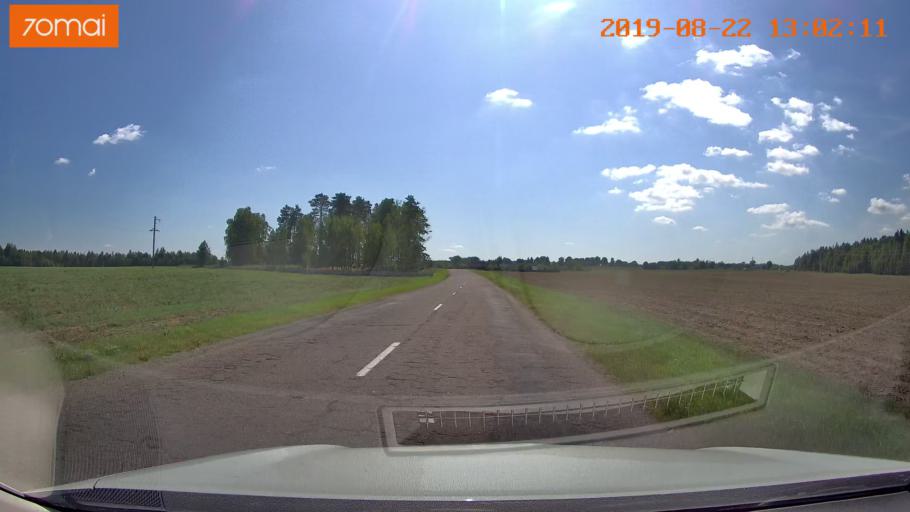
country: BY
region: Minsk
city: Prawdzinski
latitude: 53.3917
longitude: 27.8242
